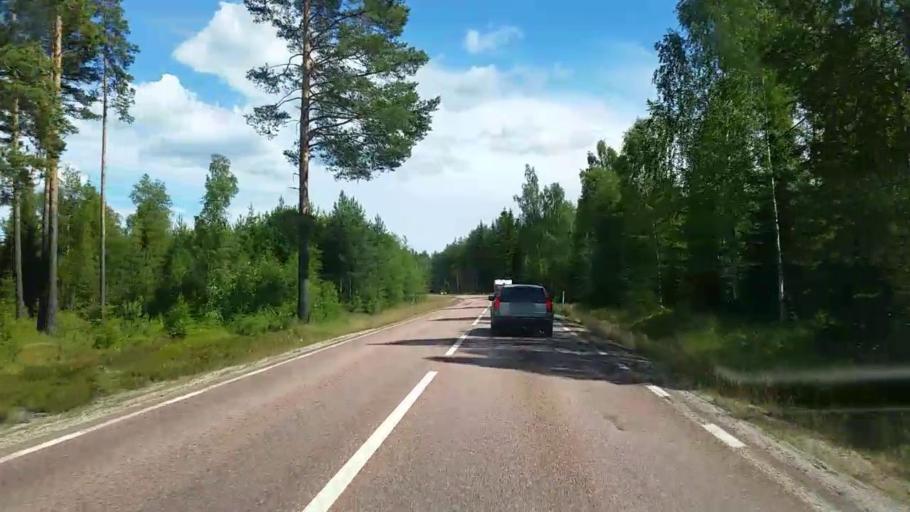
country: SE
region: Gaevleborg
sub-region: Ovanakers Kommun
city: Edsbyn
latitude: 61.3453
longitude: 15.6607
